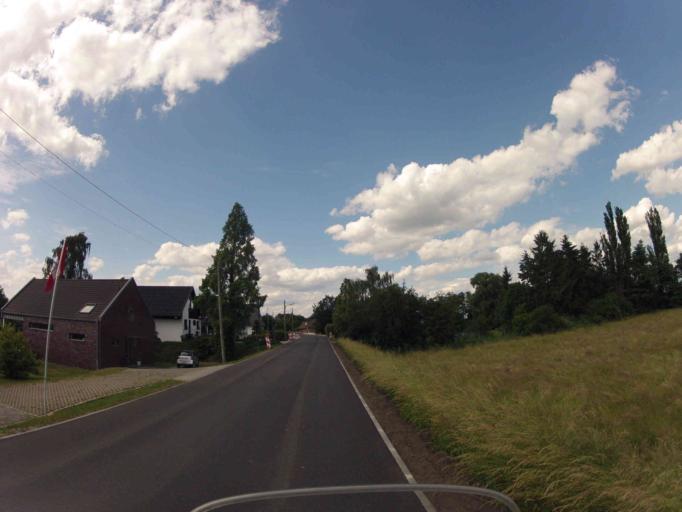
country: DE
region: Hamburg
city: Bergedorf
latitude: 53.4502
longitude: 10.1577
